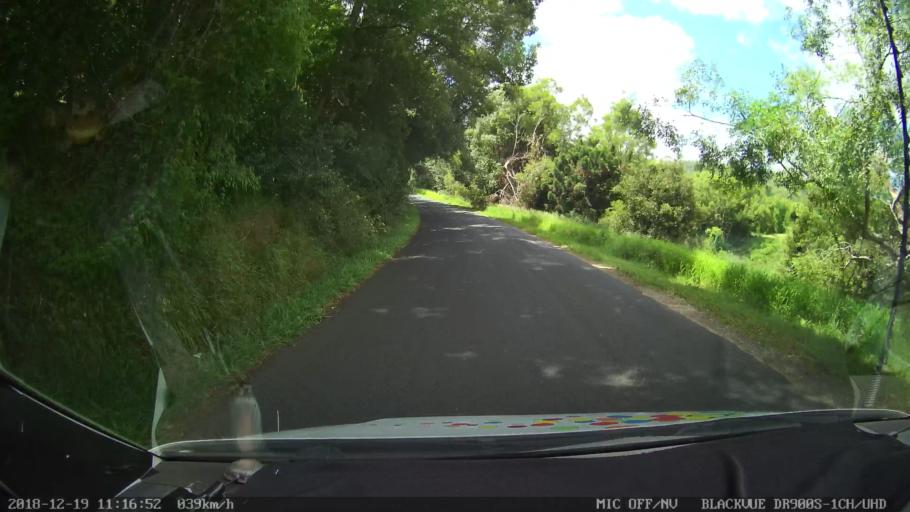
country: AU
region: New South Wales
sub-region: Lismore Municipality
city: Nimbin
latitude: -28.6760
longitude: 153.2788
